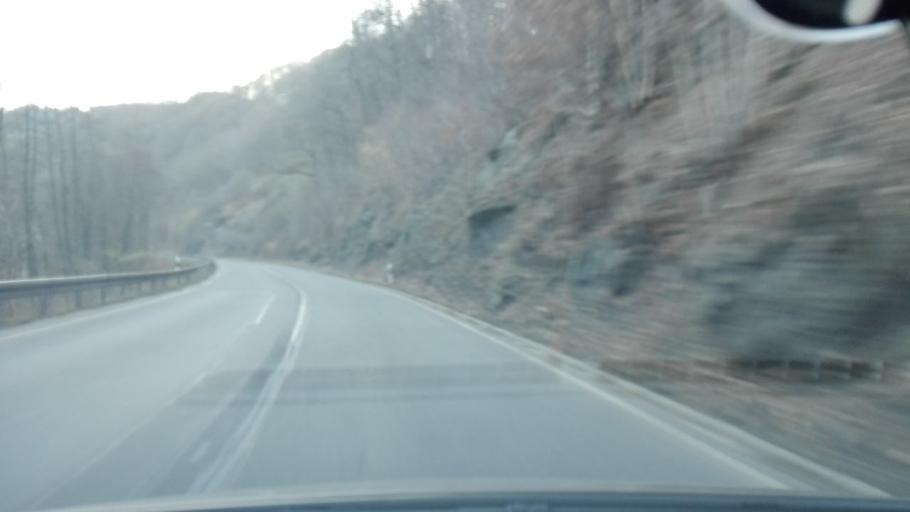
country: DE
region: North Rhine-Westphalia
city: Plettenberg
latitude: 51.2304
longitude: 7.9002
